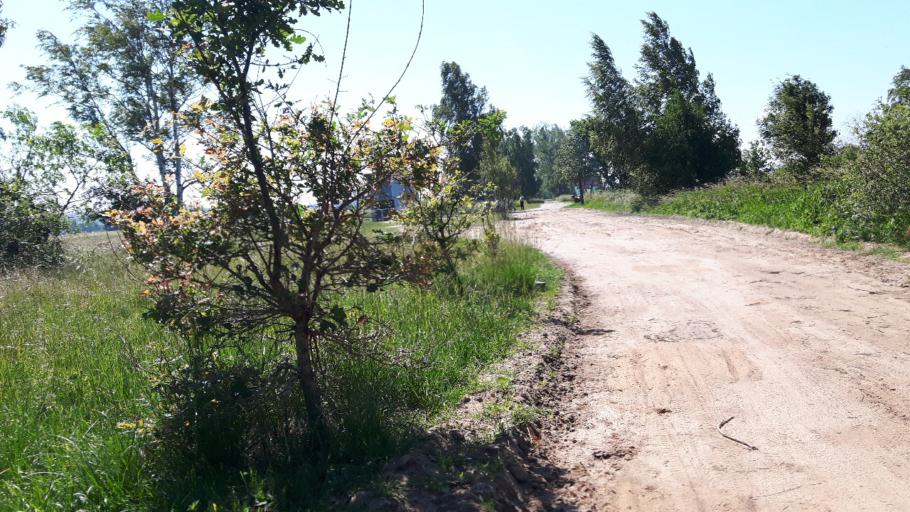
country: PL
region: Pomeranian Voivodeship
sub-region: Powiat slupski
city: Smoldzino
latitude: 54.6696
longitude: 17.1602
